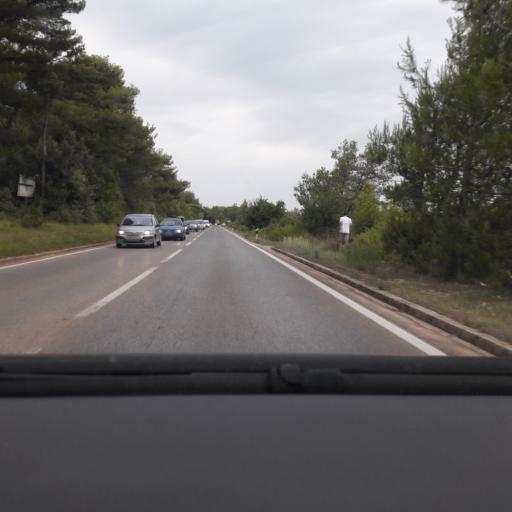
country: HR
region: Zadarska
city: Zadar
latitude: 44.1494
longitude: 15.2216
